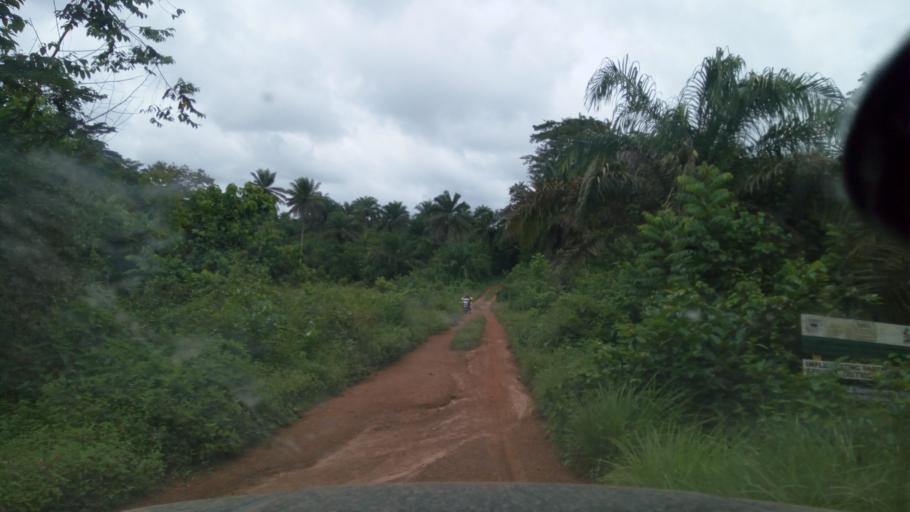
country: SL
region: Eastern Province
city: Gorahun
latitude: 7.6105
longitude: -11.2686
